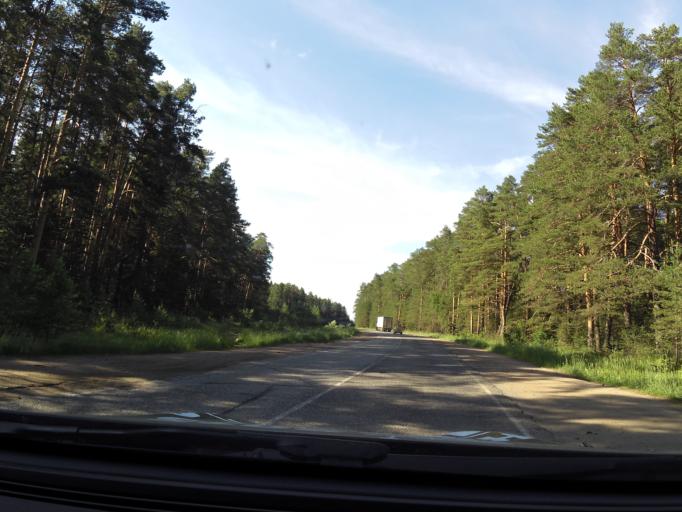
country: RU
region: Kirov
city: Belaya Kholunitsa
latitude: 58.8608
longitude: 50.8426
